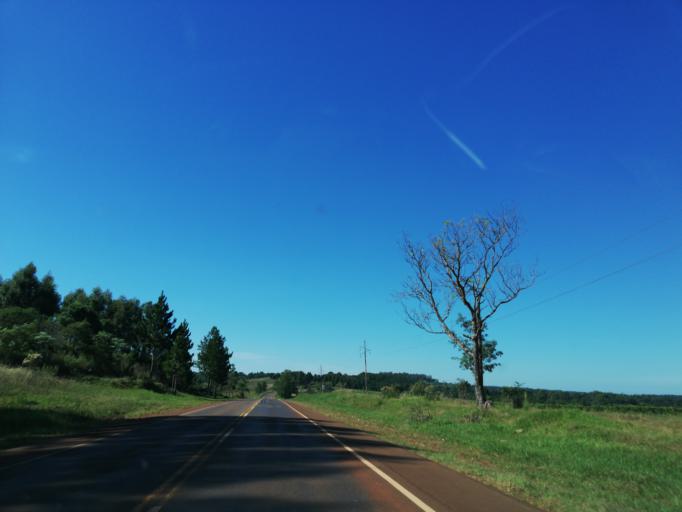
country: AR
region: Misiones
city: Dos de Mayo
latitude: -27.0749
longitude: -54.4055
